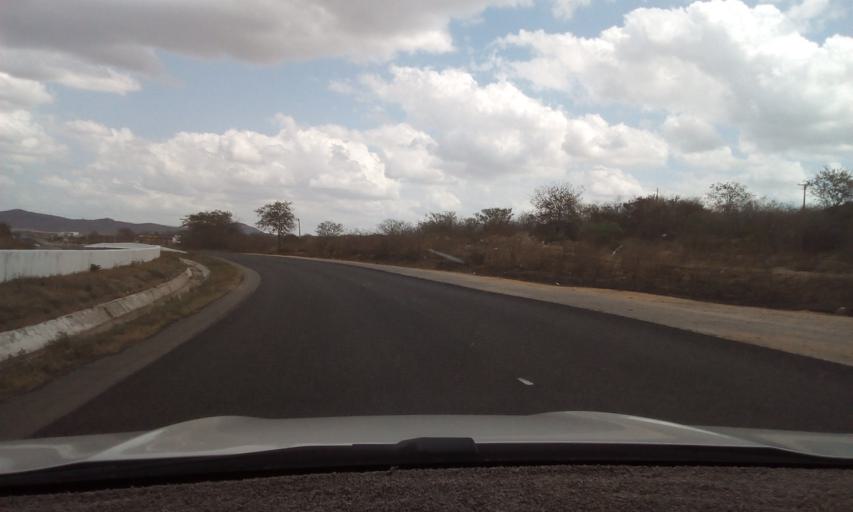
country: BR
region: Pernambuco
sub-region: Toritama
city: Toritama
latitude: -8.0955
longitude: -36.0334
